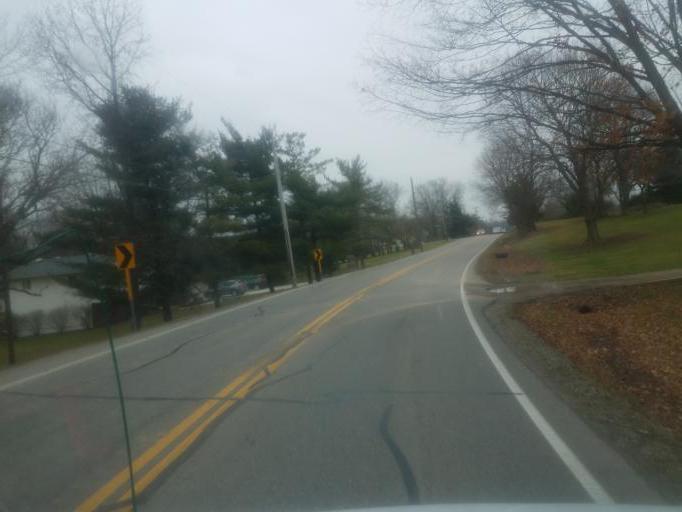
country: US
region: Ohio
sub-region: Franklin County
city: Westerville
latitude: 40.1557
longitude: -82.9459
